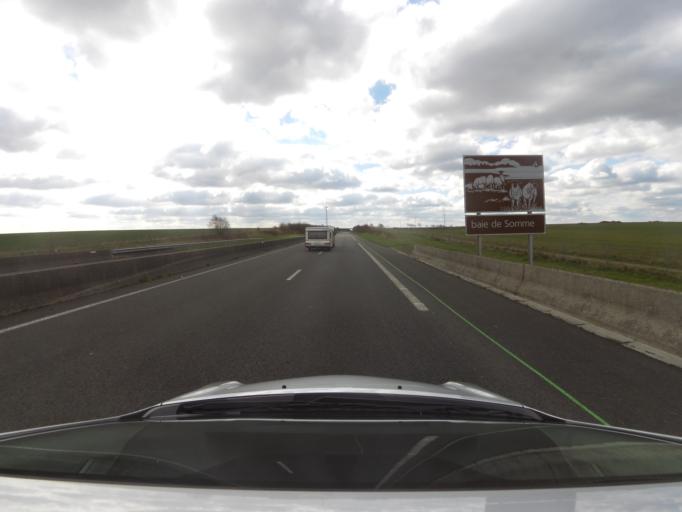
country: FR
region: Picardie
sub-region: Departement de la Somme
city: Nouvion
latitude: 50.2100
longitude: 1.7553
